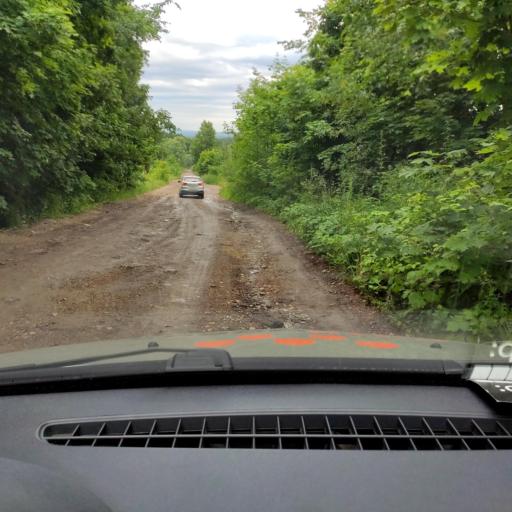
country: RU
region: Bashkortostan
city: Iglino
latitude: 54.8891
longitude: 56.2739
